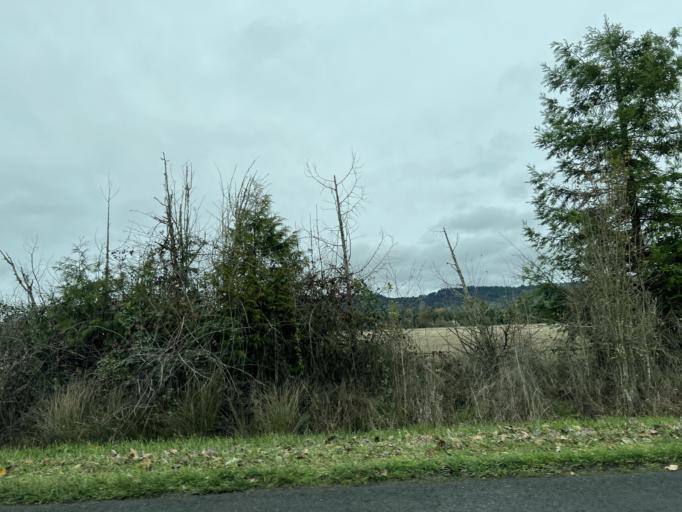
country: US
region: Oregon
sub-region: Polk County
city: Independence
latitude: 44.8074
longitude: -123.0861
